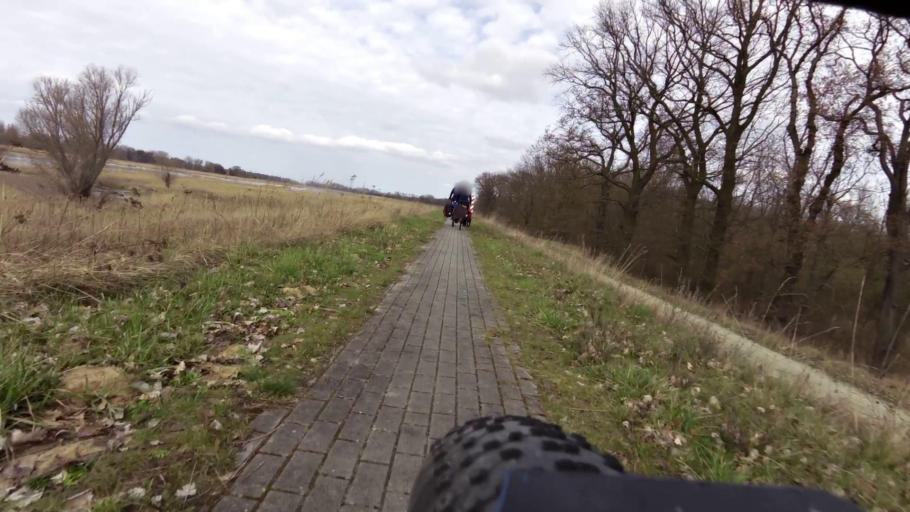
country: PL
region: Lubusz
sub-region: Powiat slubicki
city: Gorzyca
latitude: 52.4835
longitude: 14.6302
